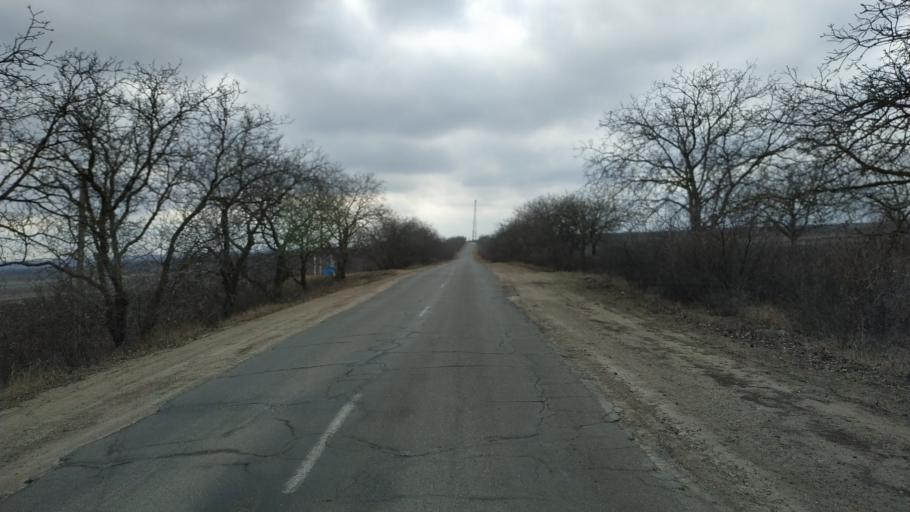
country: MD
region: Laloveni
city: Ialoveni
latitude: 46.8956
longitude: 28.7715
